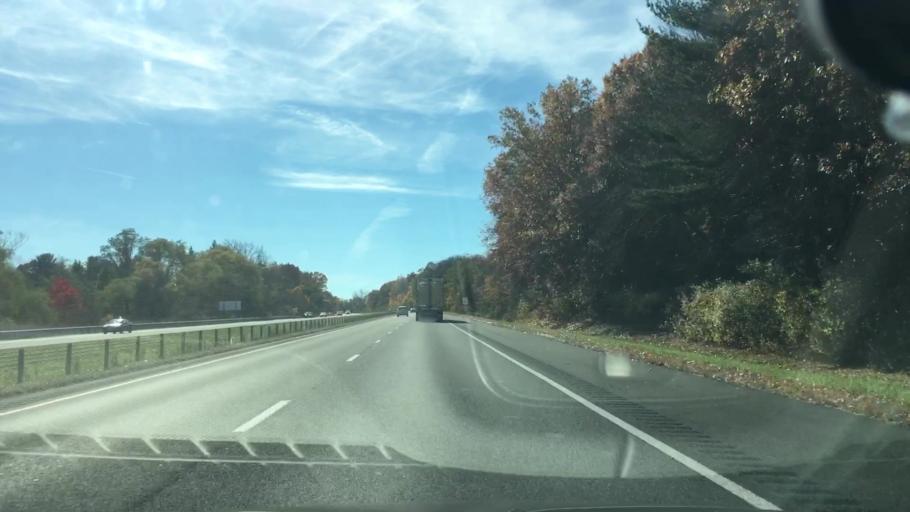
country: US
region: Massachusetts
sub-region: Hampden County
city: Holyoke
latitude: 42.2333
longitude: -72.6343
